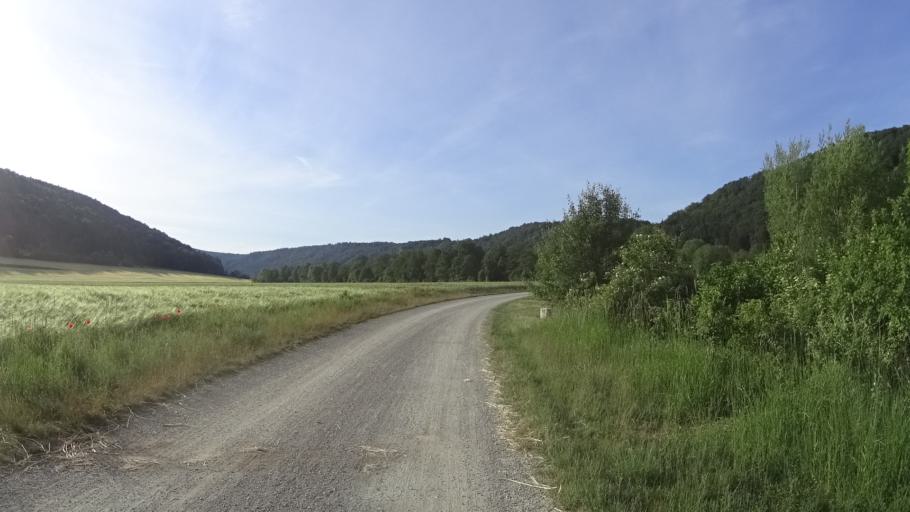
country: DE
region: Bavaria
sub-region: Lower Bavaria
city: Riedenburg
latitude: 48.9826
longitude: 11.6358
